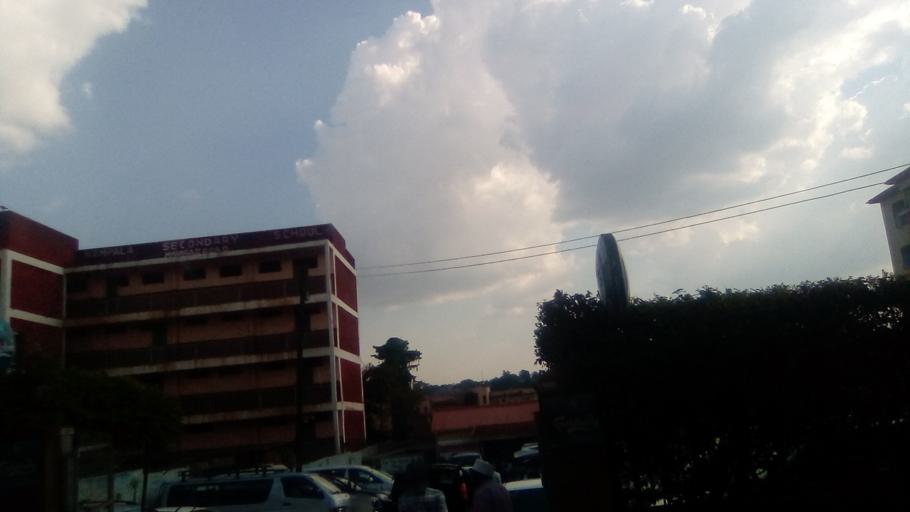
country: UG
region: Central Region
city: Kampala Central Division
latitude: 0.3122
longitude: 32.5680
